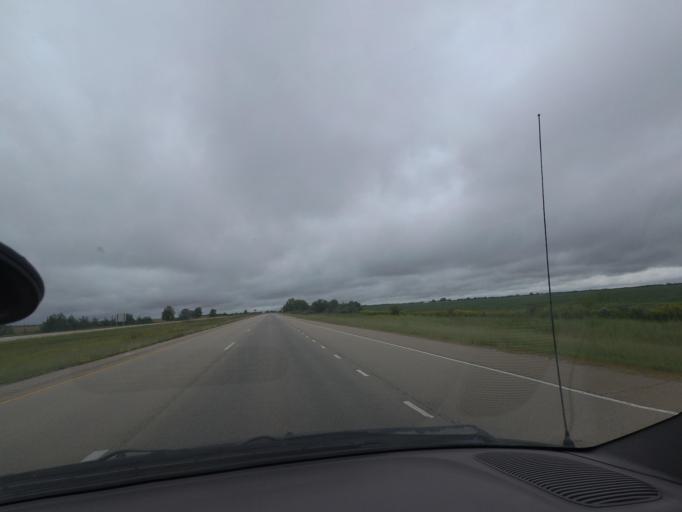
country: US
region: Illinois
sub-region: Piatt County
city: Cerro Gordo
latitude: 39.9599
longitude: -88.8195
